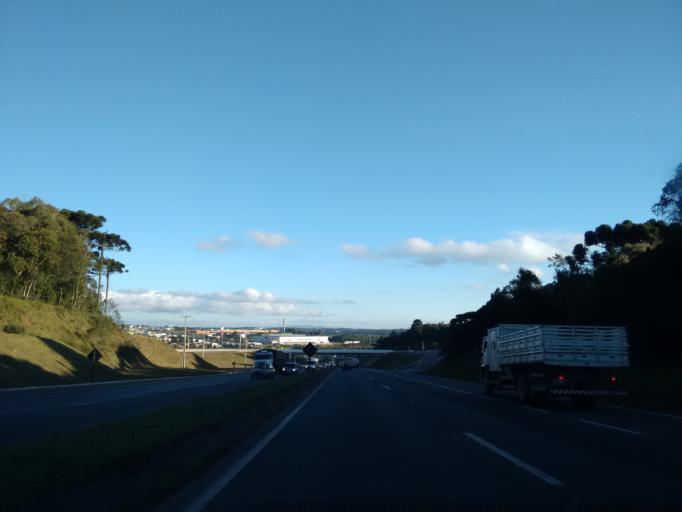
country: BR
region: Parana
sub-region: Sao Jose Dos Pinhais
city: Sao Jose dos Pinhais
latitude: -25.5914
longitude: -49.1718
